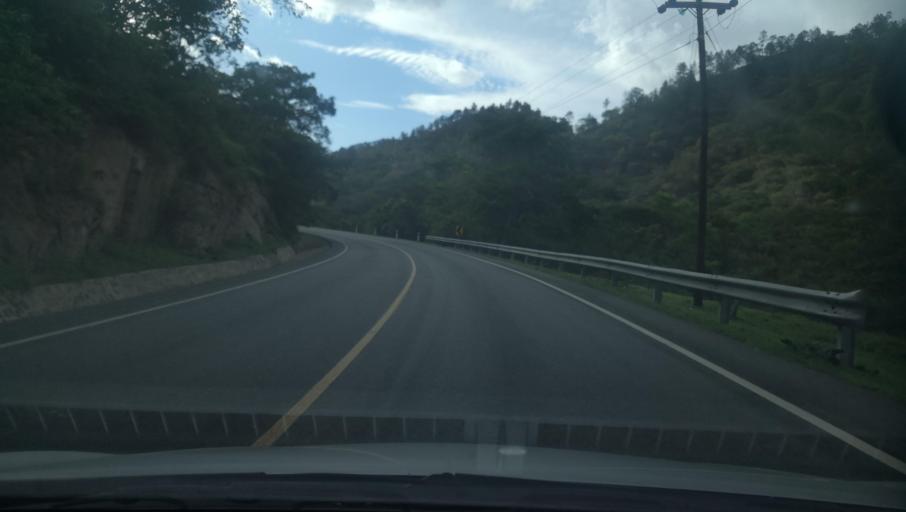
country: NI
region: Nueva Segovia
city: Mozonte
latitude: 13.6979
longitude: -86.4879
